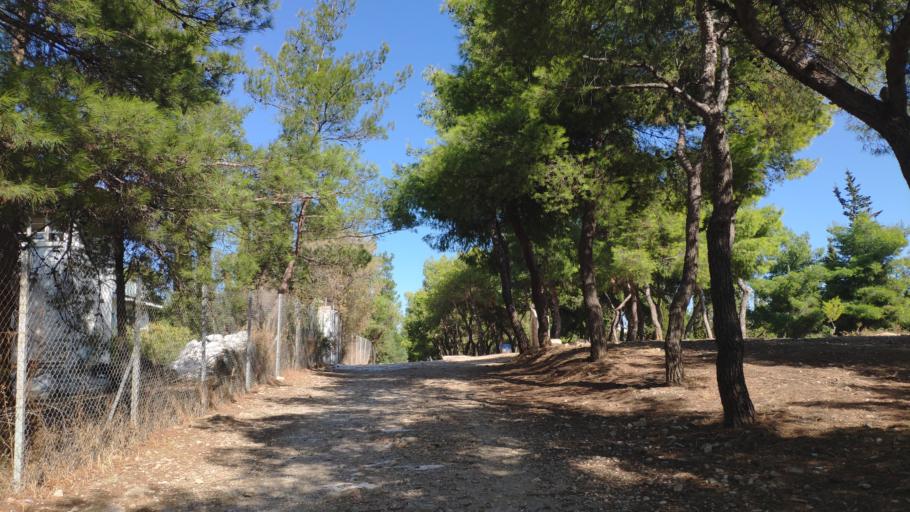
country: GR
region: Attica
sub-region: Nomarchia Athinas
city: Nea Filadelfeia
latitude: 38.0450
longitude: 23.7461
